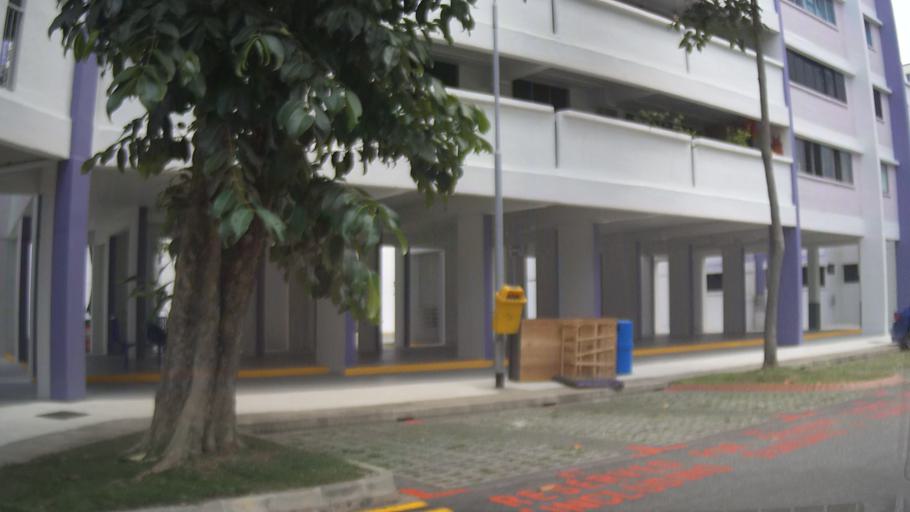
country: SG
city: Singapore
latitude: 1.3232
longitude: 103.8635
